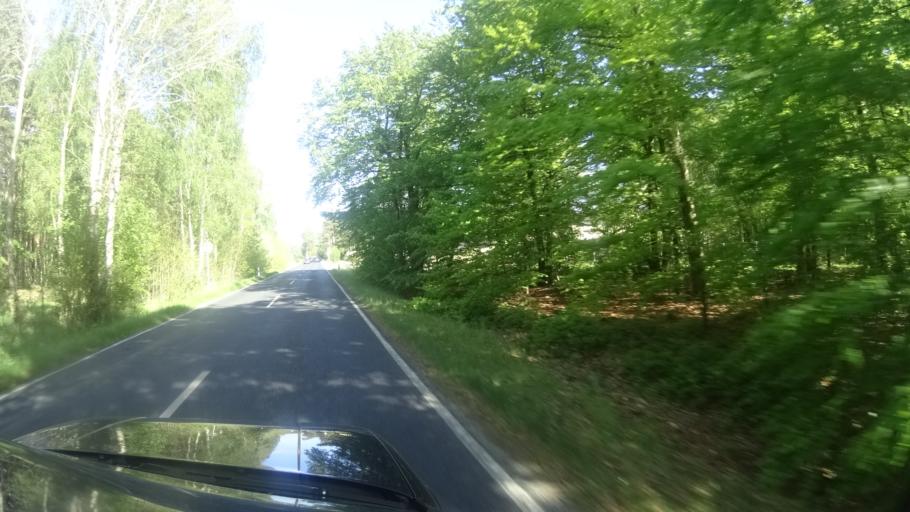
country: DE
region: Mecklenburg-Vorpommern
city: Seeheilbad Graal-Muritz
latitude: 54.2582
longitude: 12.2800
